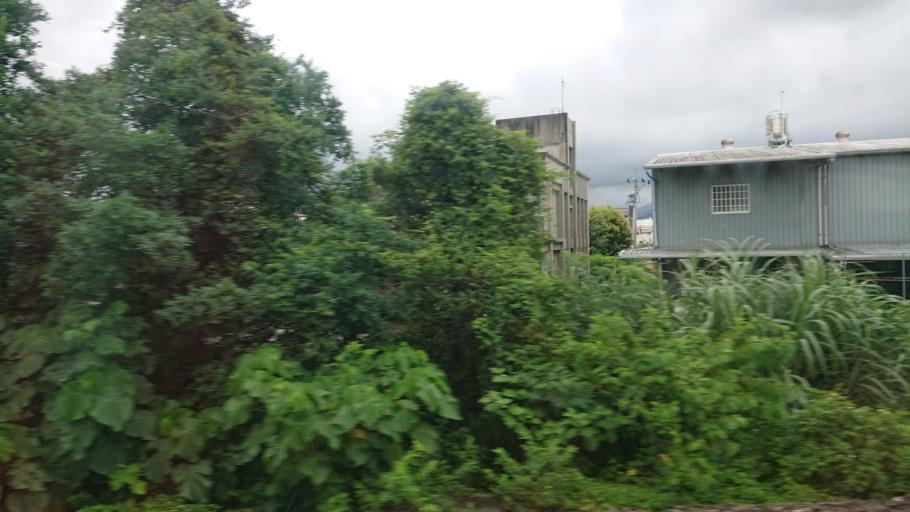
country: TW
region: Taiwan
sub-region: Yilan
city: Yilan
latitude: 24.7753
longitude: 121.7608
